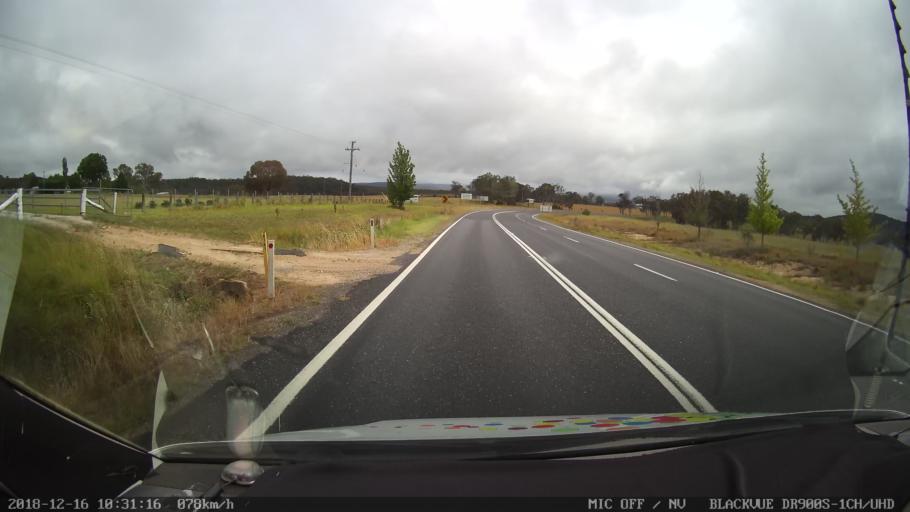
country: AU
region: New South Wales
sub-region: Tenterfield Municipality
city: Carrolls Creek
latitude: -29.0829
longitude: 152.0045
